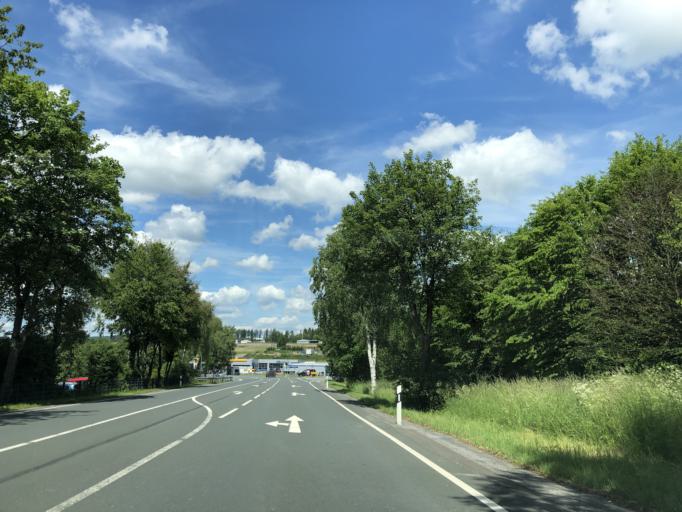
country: DE
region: North Rhine-Westphalia
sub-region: Regierungsbezirk Arnsberg
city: Erndtebruck
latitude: 50.9944
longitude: 8.3124
